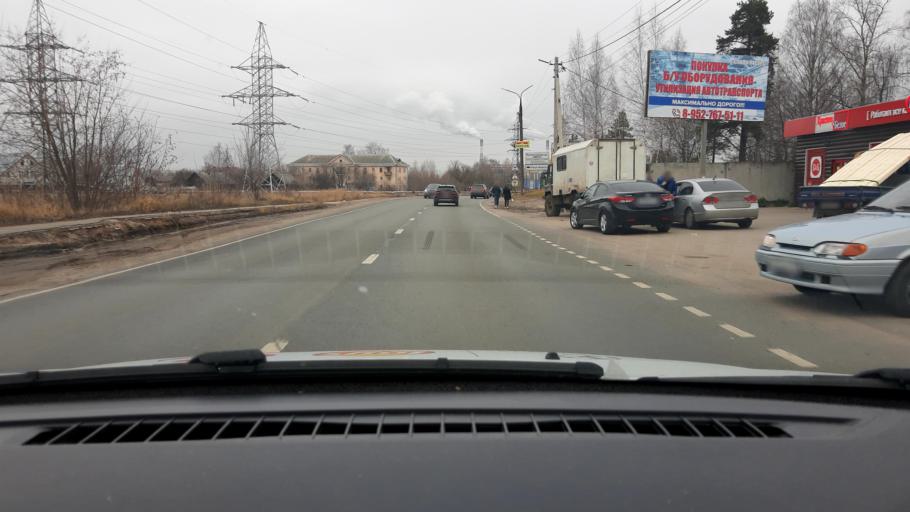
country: RU
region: Nizjnij Novgorod
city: Novaya Balakhna
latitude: 56.4858
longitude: 43.5981
